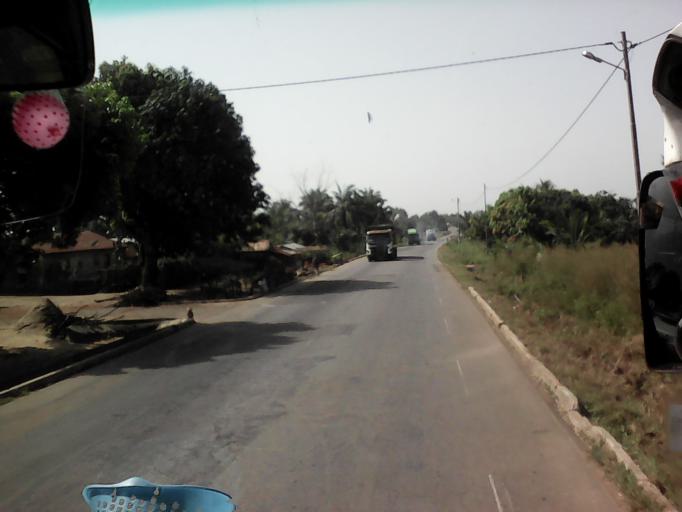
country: TG
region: Centrale
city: Sokode
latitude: 8.8033
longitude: 1.0727
